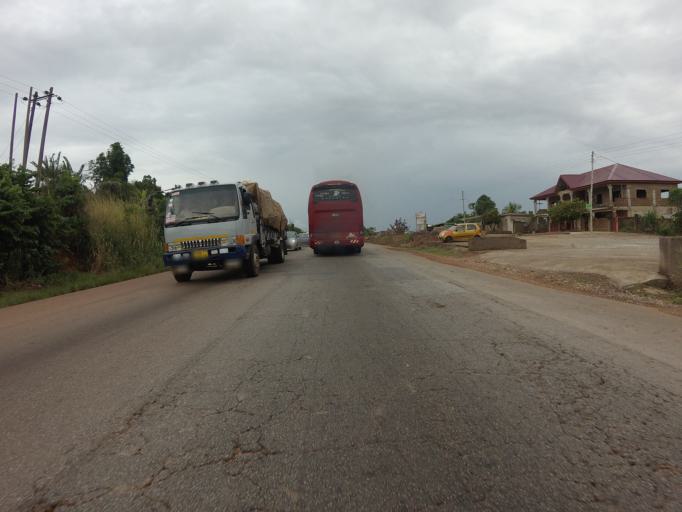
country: GH
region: Ashanti
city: Konongo
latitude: 6.6173
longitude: -1.1812
